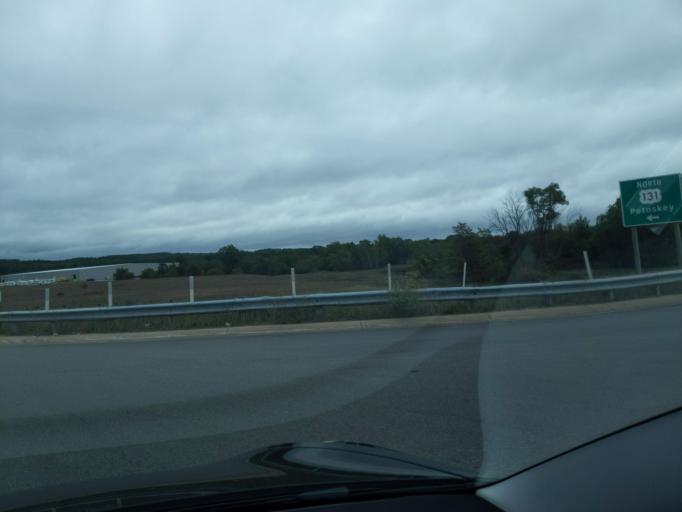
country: US
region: Michigan
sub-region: Wexford County
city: Cadillac
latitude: 44.2815
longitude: -85.3860
